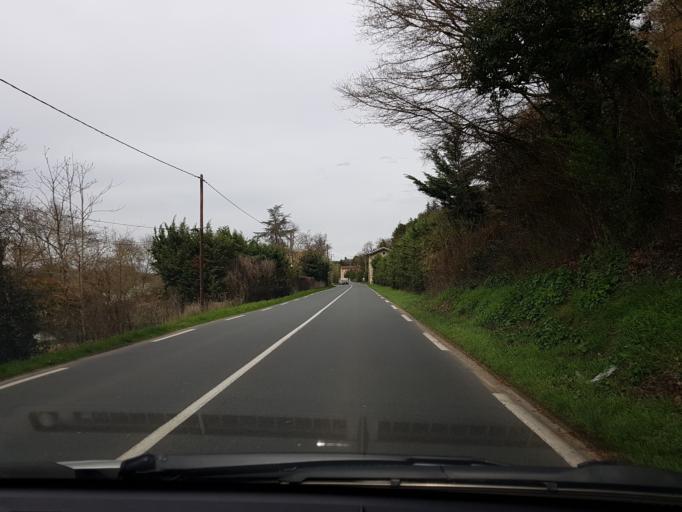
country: FR
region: Rhone-Alpes
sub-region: Departement de l'Ain
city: Jassans-Riottier
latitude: 45.9653
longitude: 4.7534
